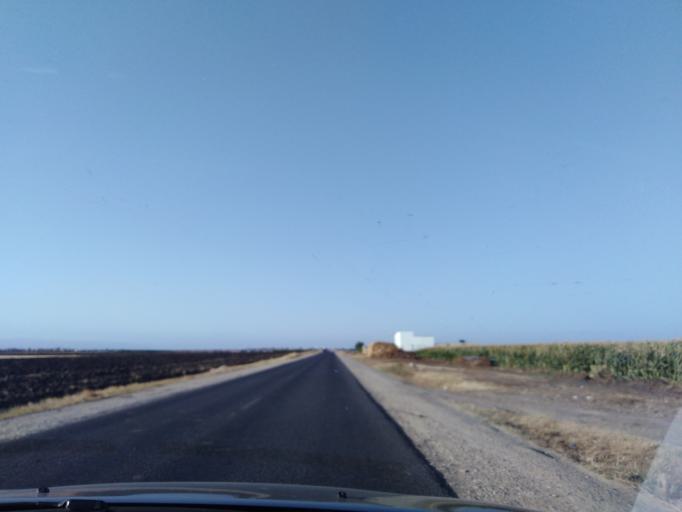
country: MA
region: Doukkala-Abda
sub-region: Safi
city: Safi
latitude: 32.5098
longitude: -8.9182
